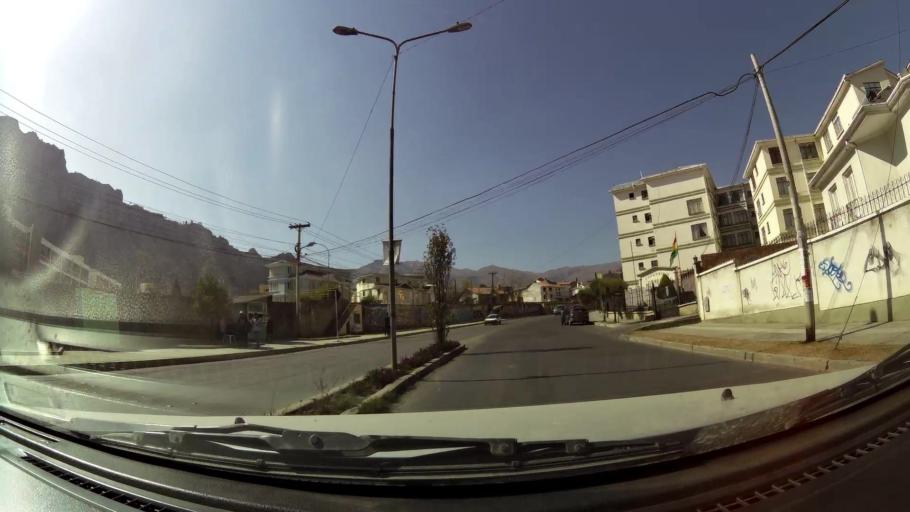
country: BO
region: La Paz
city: La Paz
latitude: -16.5235
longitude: -68.0666
